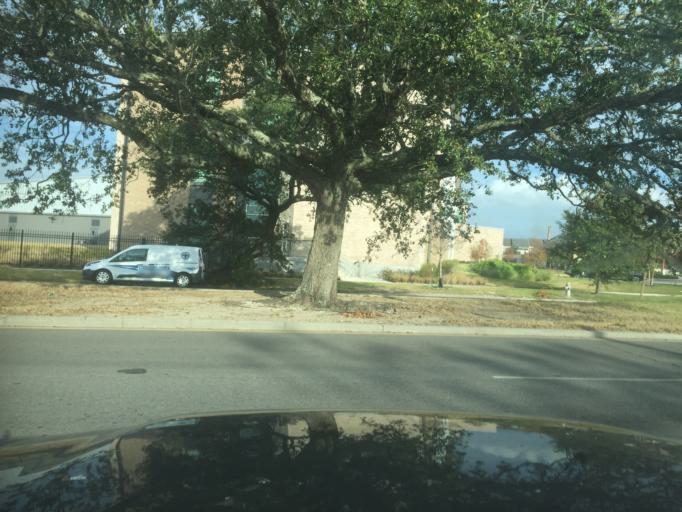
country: US
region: Louisiana
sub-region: Orleans Parish
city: New Orleans
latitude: 29.9964
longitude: -90.0794
